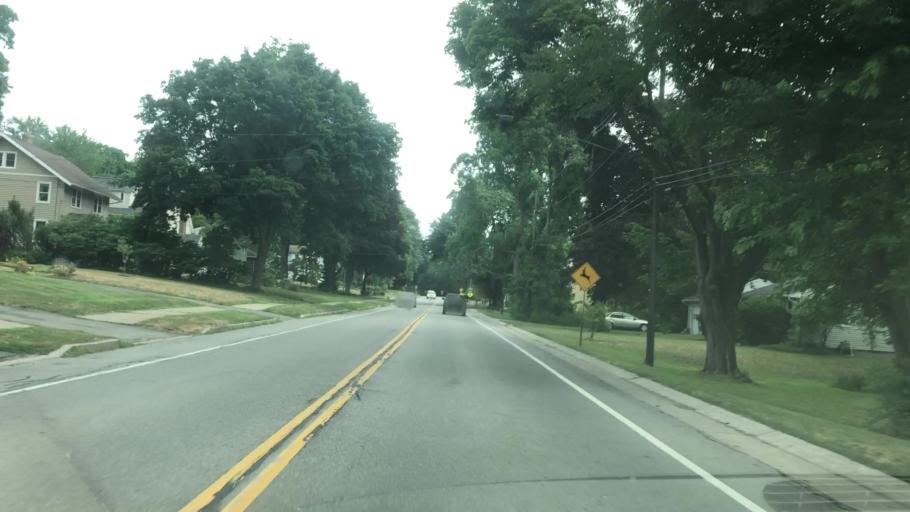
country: US
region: New York
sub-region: Monroe County
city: East Rochester
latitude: 43.1263
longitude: -77.4760
